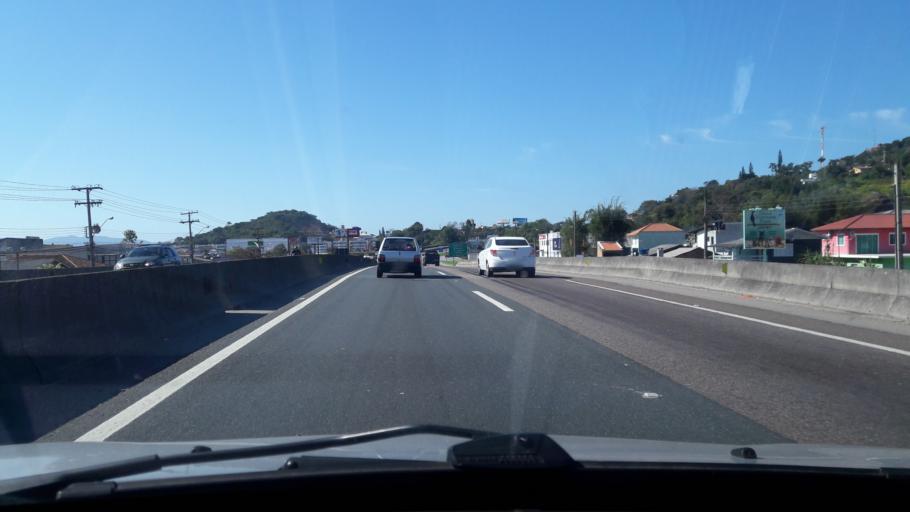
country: BR
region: Santa Catarina
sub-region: Biguacu
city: Biguacu
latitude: -27.5114
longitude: -48.6427
